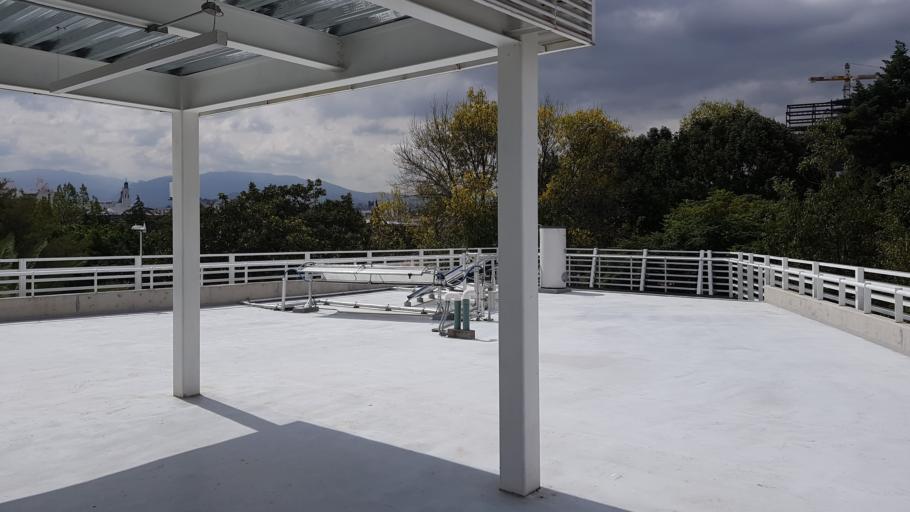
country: MX
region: Mexico City
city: Colonia del Valle
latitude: 19.3739
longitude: -99.1836
